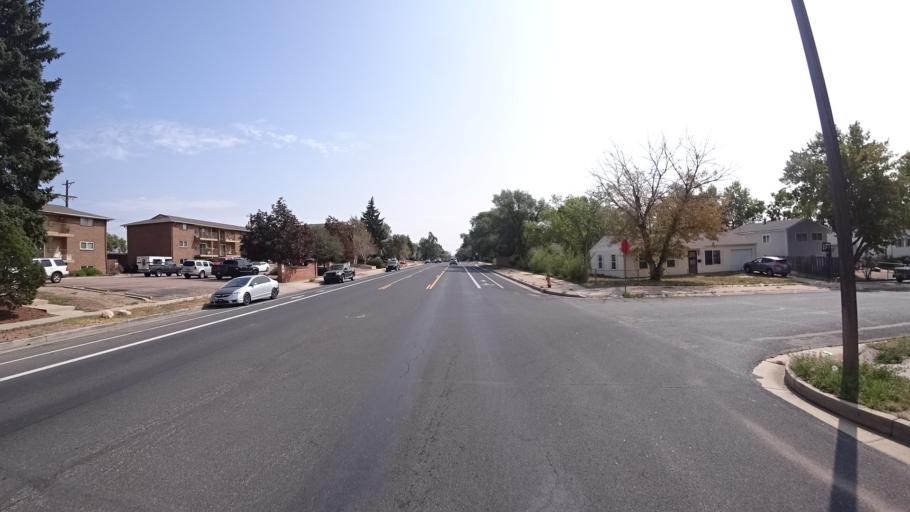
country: US
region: Colorado
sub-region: El Paso County
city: Colorado Springs
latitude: 38.8358
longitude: -104.7732
